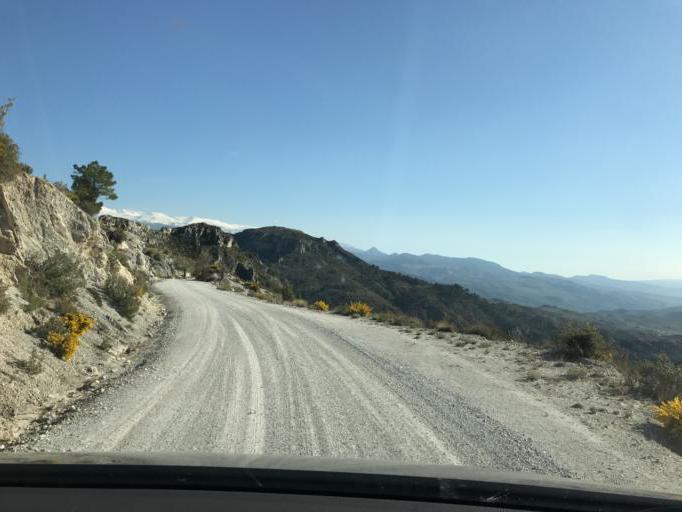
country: ES
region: Andalusia
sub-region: Provincia de Granada
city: Beas de Granada
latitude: 37.2453
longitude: -3.4567
